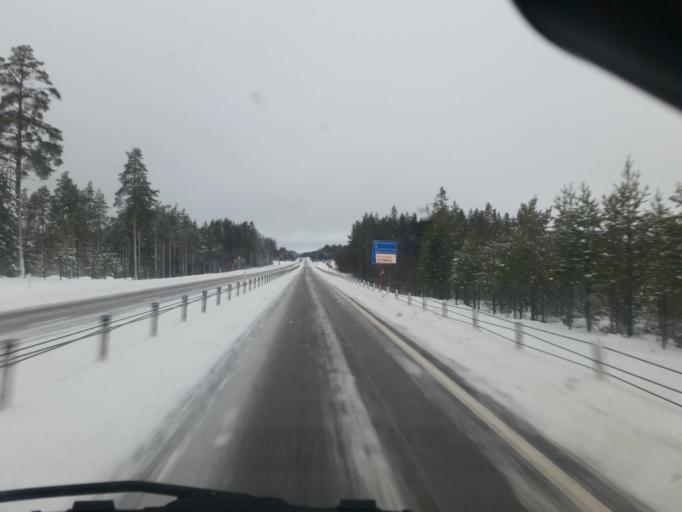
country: SE
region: Norrbotten
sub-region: Pitea Kommun
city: Pitea
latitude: 65.2239
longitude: 21.5147
